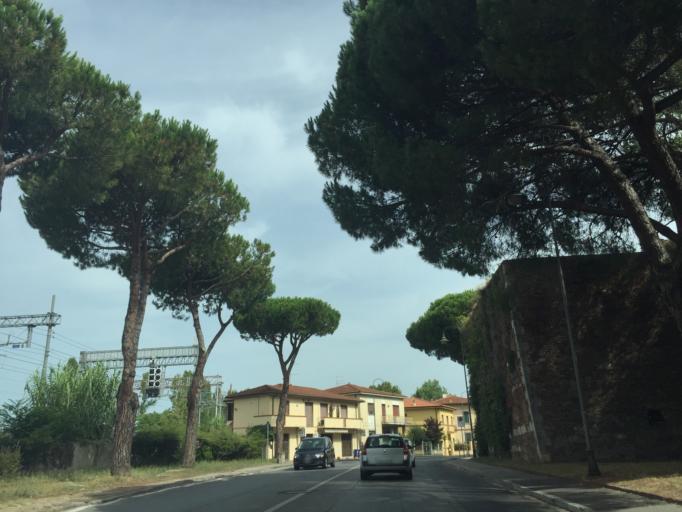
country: IT
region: Tuscany
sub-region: Province of Pisa
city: Pisa
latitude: 43.7150
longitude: 10.3881
